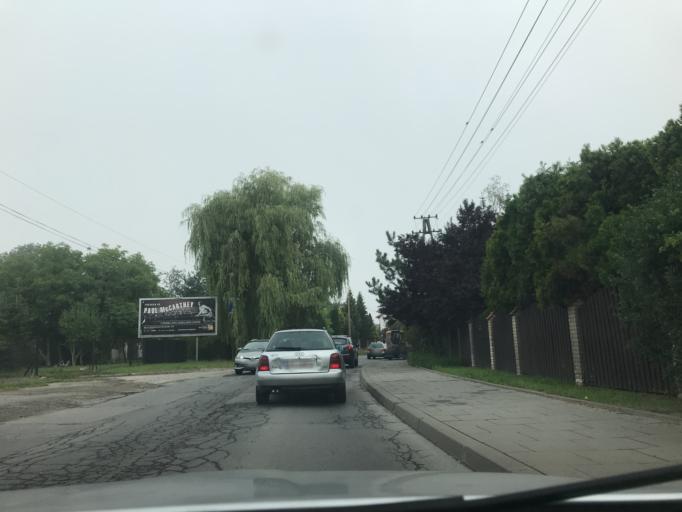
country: PL
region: Lesser Poland Voivodeship
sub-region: Powiat krakowski
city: Ochojno
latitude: 50.0041
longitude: 19.9880
